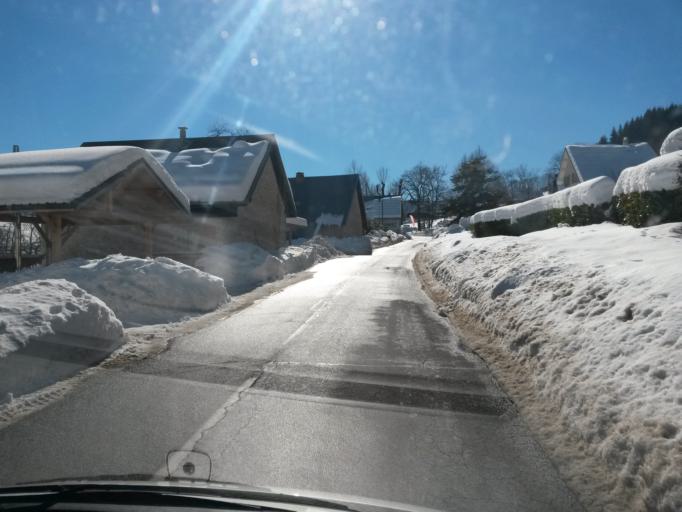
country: FR
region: Rhone-Alpes
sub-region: Departement de l'Isere
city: Saint-Hilaire
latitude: 45.3141
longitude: 5.8878
